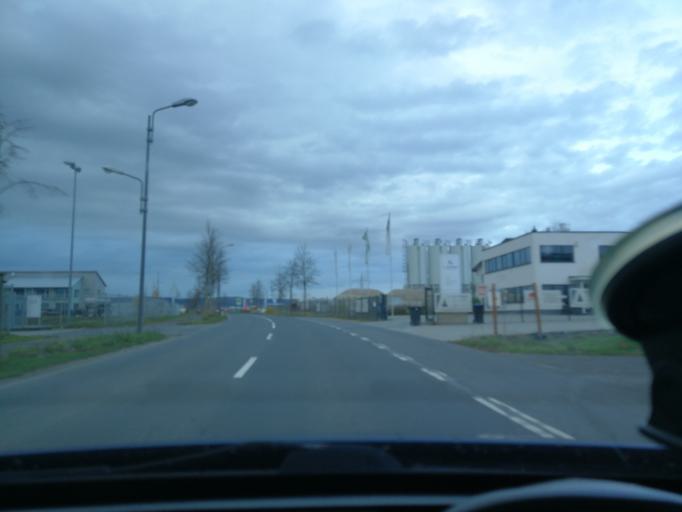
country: DE
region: Rheinland-Pfalz
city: Platten
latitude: 49.9674
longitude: 6.9478
